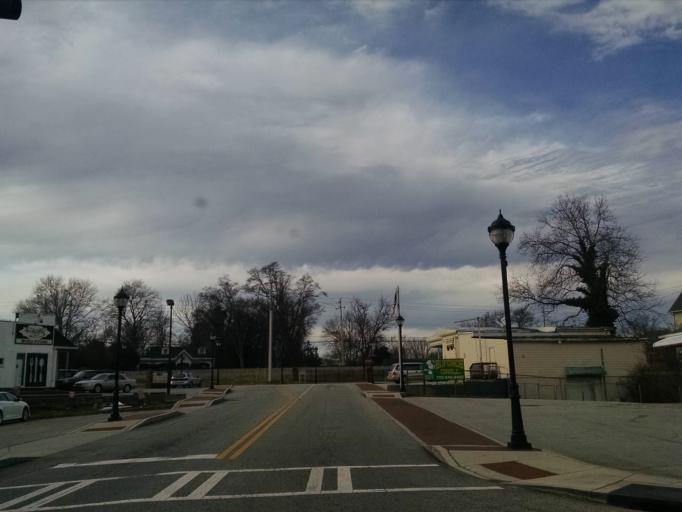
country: US
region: Georgia
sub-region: Gwinnett County
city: Buford
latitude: 34.1168
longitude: -84.0093
